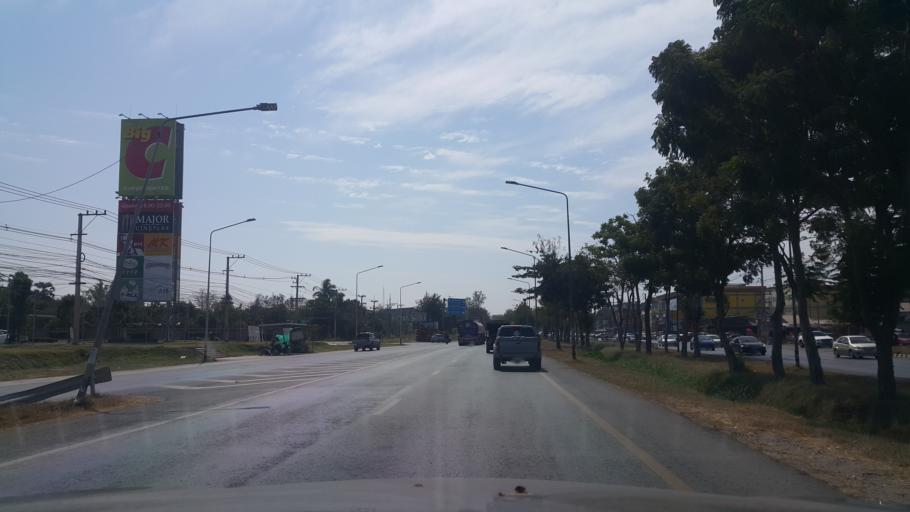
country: TH
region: Nakhon Ratchasima
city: Nakhon Ratchasima
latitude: 14.9496
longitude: 102.0539
